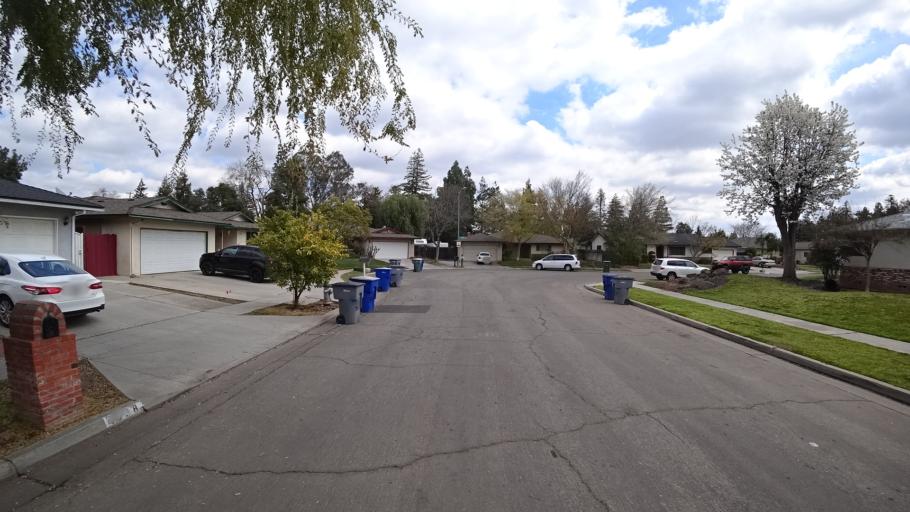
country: US
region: California
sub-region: Fresno County
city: Fresno
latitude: 36.8367
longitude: -119.8227
